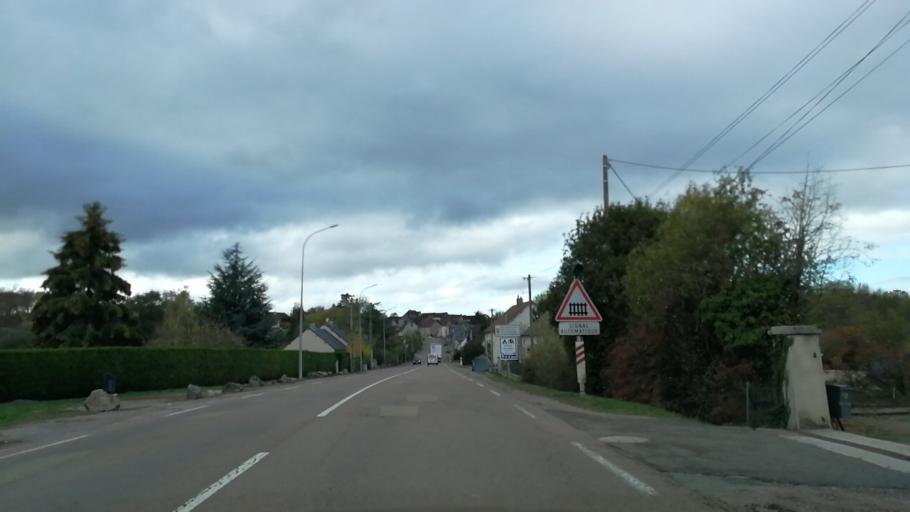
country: FR
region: Bourgogne
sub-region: Departement de la Cote-d'Or
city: Saulieu
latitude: 47.2761
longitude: 4.2417
